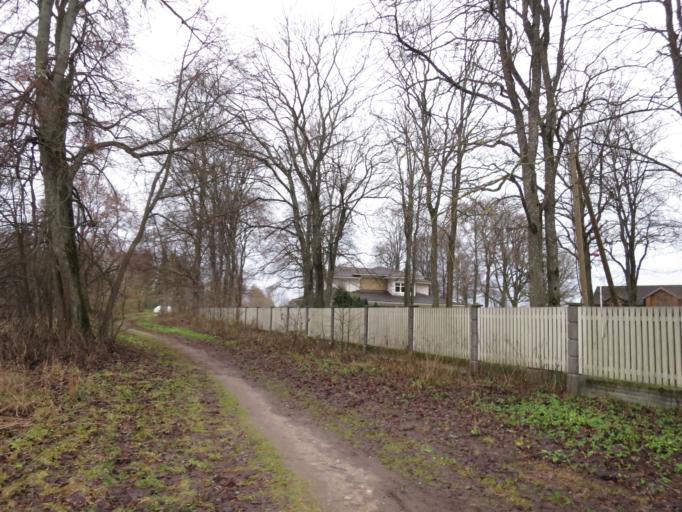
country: LV
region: Adazi
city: Adazi
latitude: 57.0744
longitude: 24.3442
